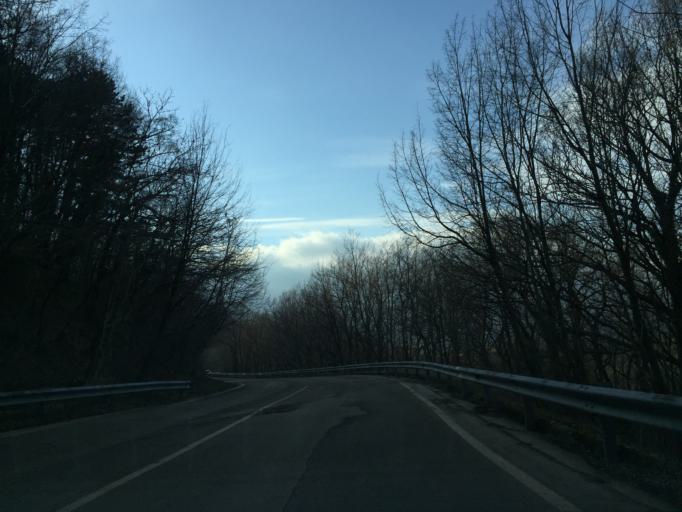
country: IT
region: Molise
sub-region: Provincia di Campobasso
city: San Massimo
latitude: 41.4783
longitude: 14.4103
